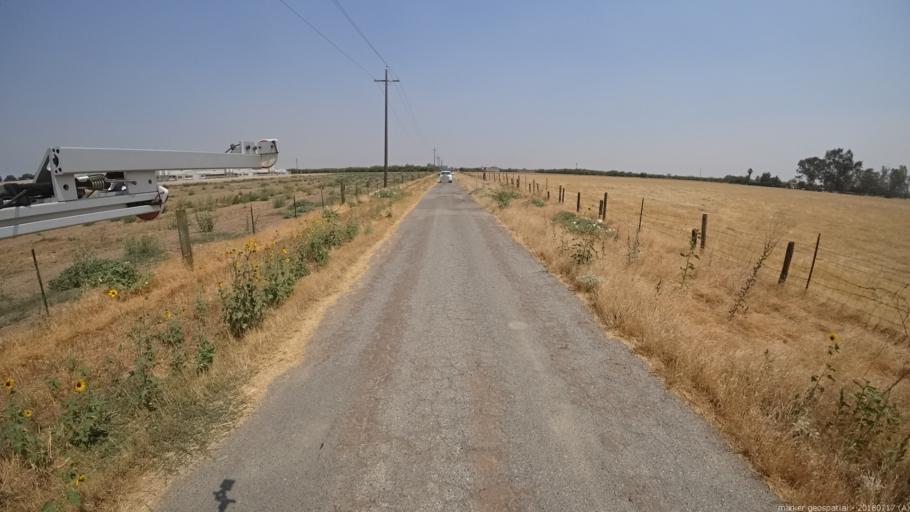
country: US
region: California
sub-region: Madera County
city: Fairmead
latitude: 37.1319
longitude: -120.1471
